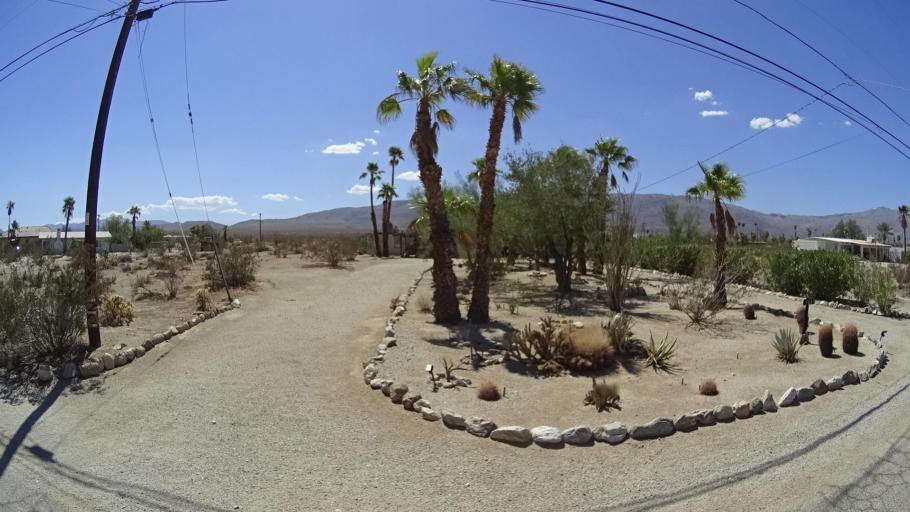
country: US
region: California
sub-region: San Diego County
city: Borrego Springs
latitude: 33.2082
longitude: -116.3323
